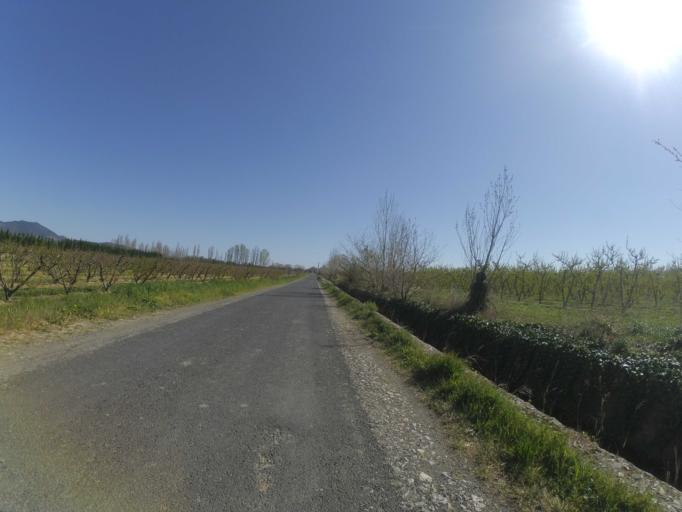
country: FR
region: Languedoc-Roussillon
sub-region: Departement des Pyrenees-Orientales
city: Millas
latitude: 42.6774
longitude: 2.6708
